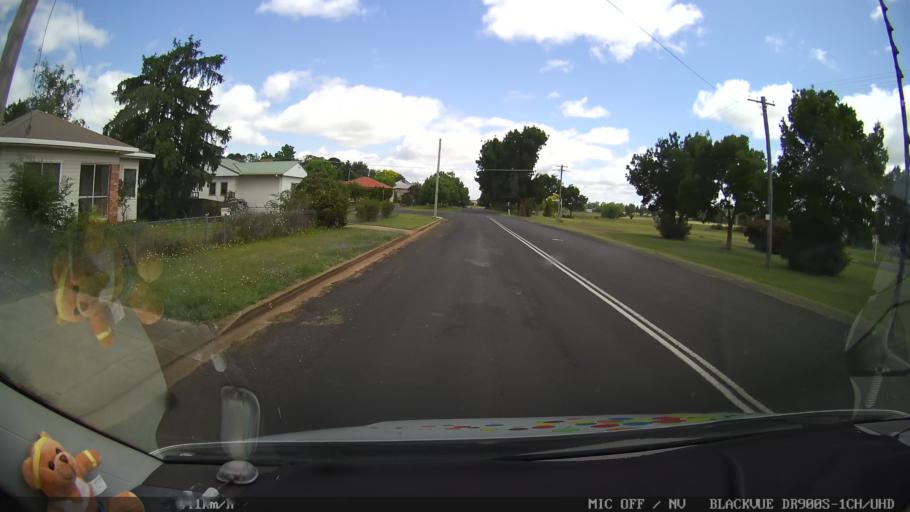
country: AU
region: New South Wales
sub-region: Glen Innes Severn
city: Glen Innes
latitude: -29.7314
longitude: 151.7335
